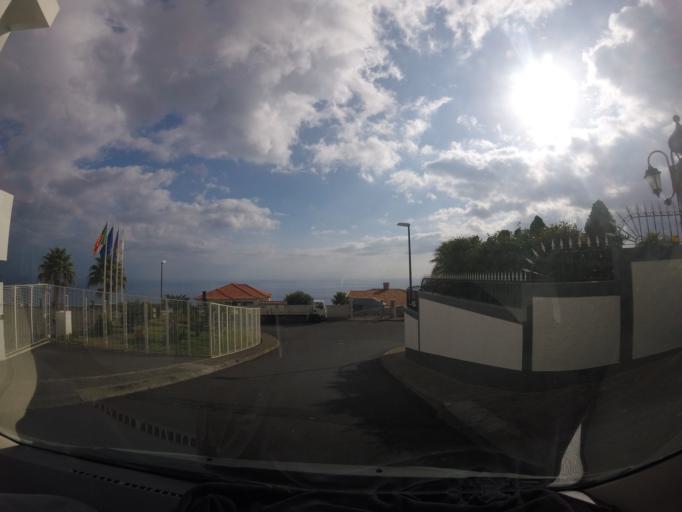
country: PT
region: Madeira
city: Canico
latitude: 32.6463
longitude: -16.8690
